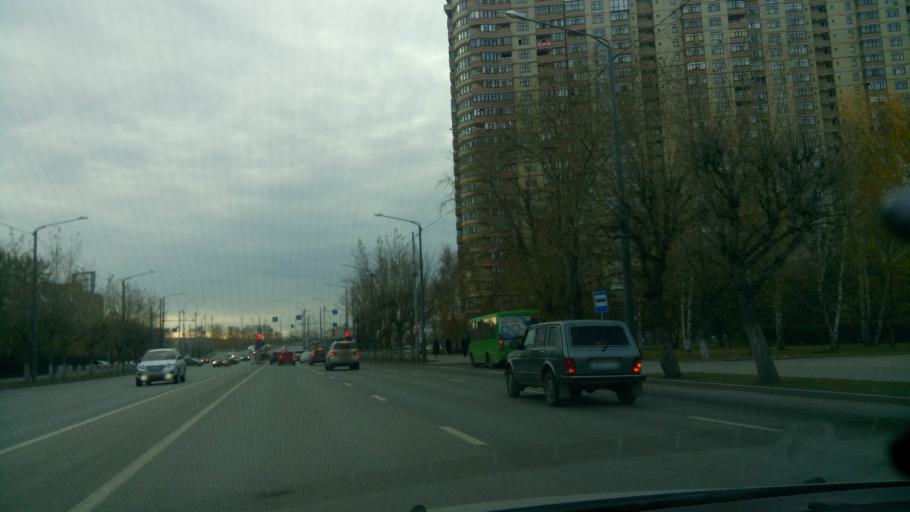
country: RU
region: Tjumen
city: Tyumen
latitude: 57.1358
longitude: 65.5660
